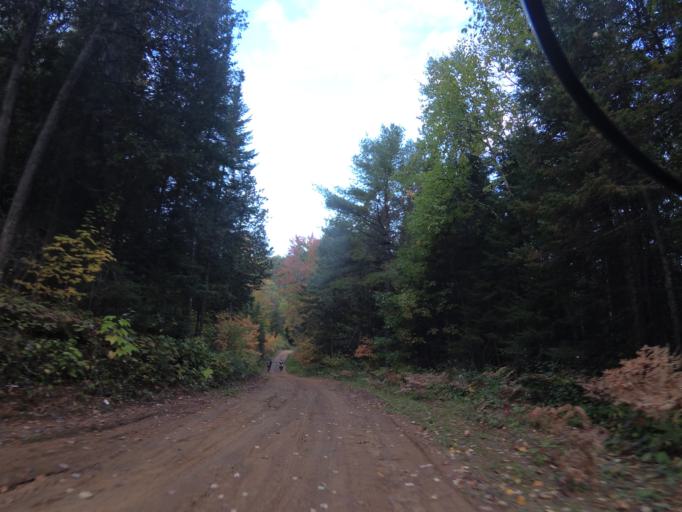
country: CA
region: Ontario
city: Pembroke
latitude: 45.3016
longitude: -77.2540
